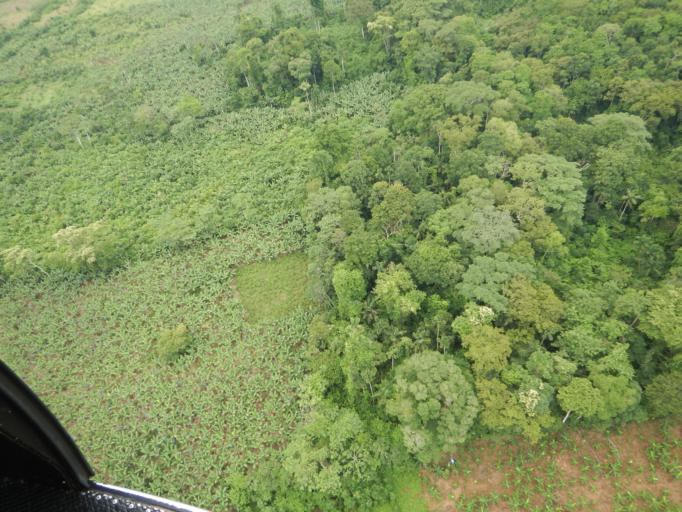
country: BO
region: Cochabamba
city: Chimore
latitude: -17.1372
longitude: -64.8126
